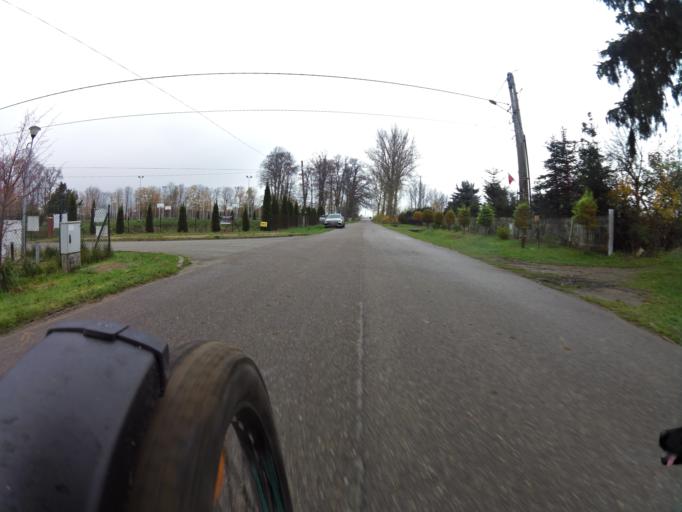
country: PL
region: Pomeranian Voivodeship
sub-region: Powiat pucki
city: Krokowa
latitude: 54.7227
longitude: 18.1380
